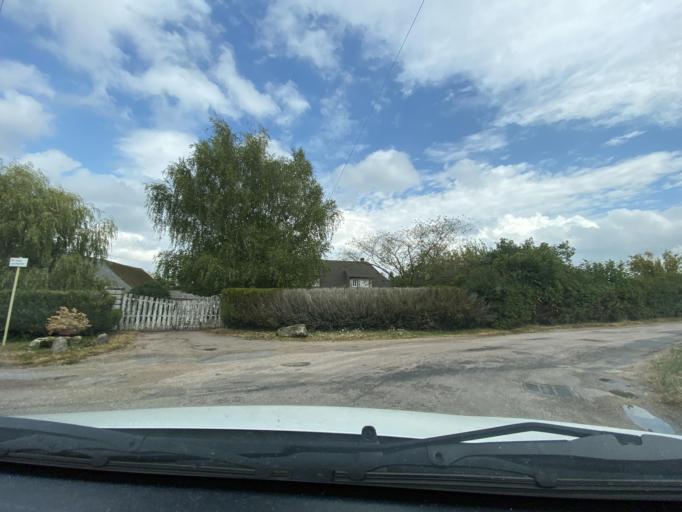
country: FR
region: Bourgogne
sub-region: Departement de la Cote-d'Or
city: Saulieu
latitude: 47.2906
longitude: 4.2390
